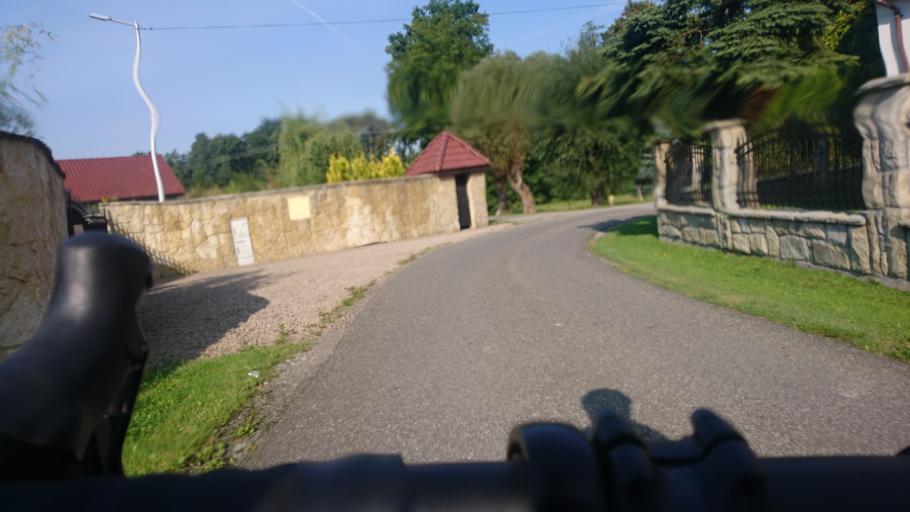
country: PL
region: Lesser Poland Voivodeship
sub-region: Powiat wadowicki
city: Sosnowice
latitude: 49.9561
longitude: 19.7075
